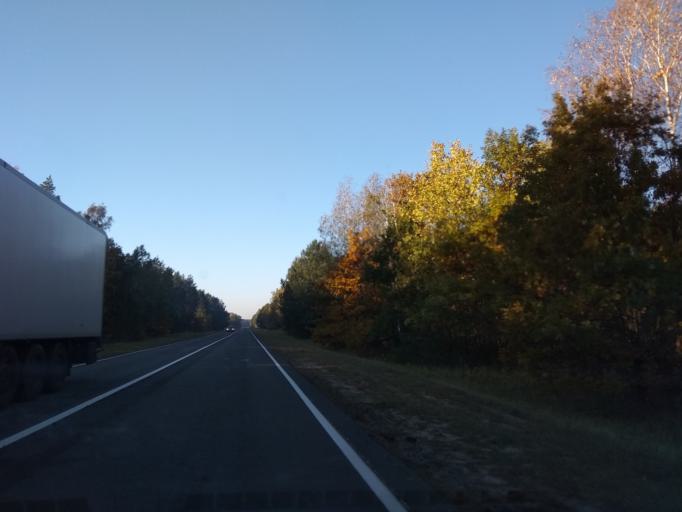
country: BY
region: Brest
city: Kobryn
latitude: 52.0235
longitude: 24.2467
